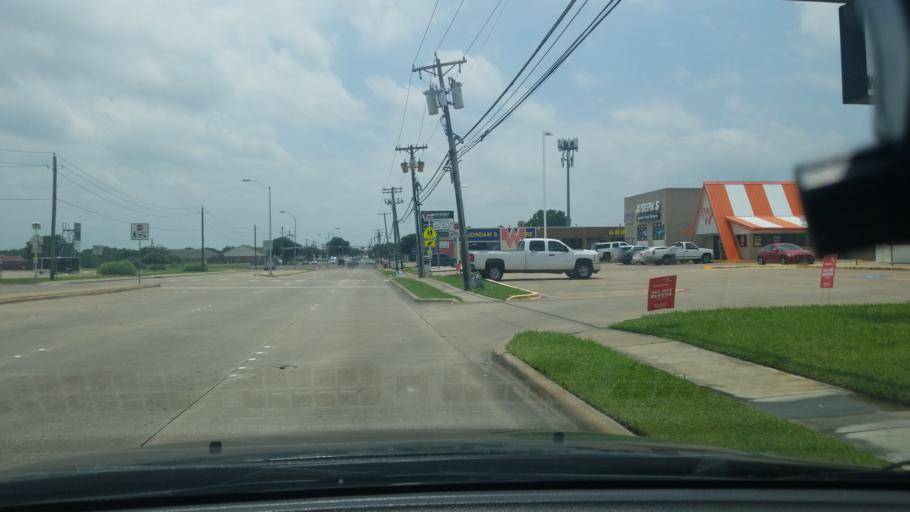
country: US
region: Texas
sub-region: Dallas County
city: Mesquite
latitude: 32.8072
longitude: -96.6113
